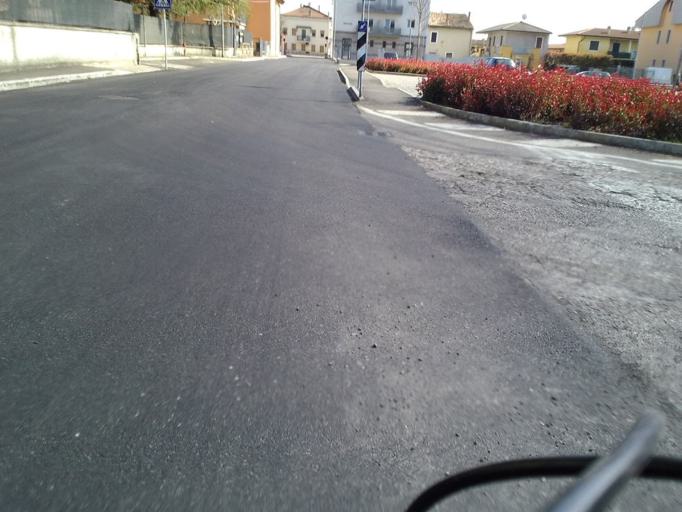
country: IT
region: Veneto
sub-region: Provincia di Verona
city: Dossobuono
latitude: 45.4068
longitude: 10.9282
